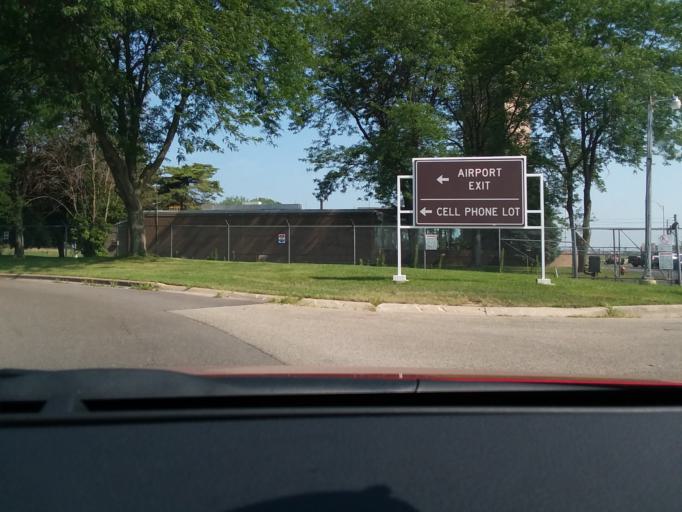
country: US
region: Wisconsin
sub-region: Dane County
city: Maple Bluff
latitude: 43.1386
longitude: -89.3464
